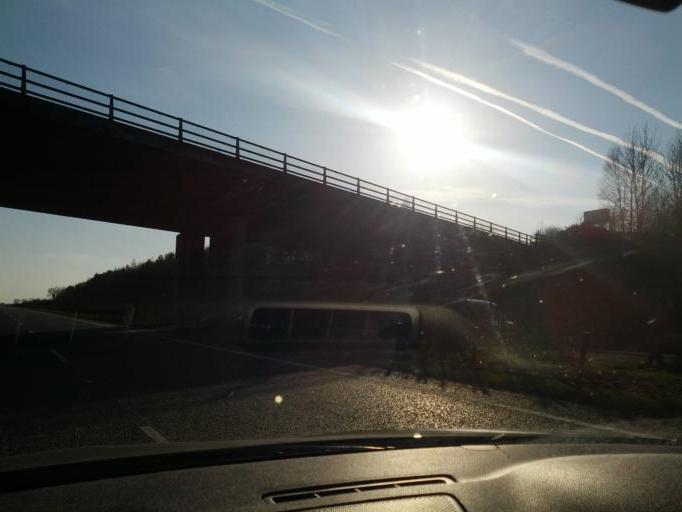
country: IE
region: Leinster
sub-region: Laois
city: Portlaoise
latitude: 53.0306
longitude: -7.2505
